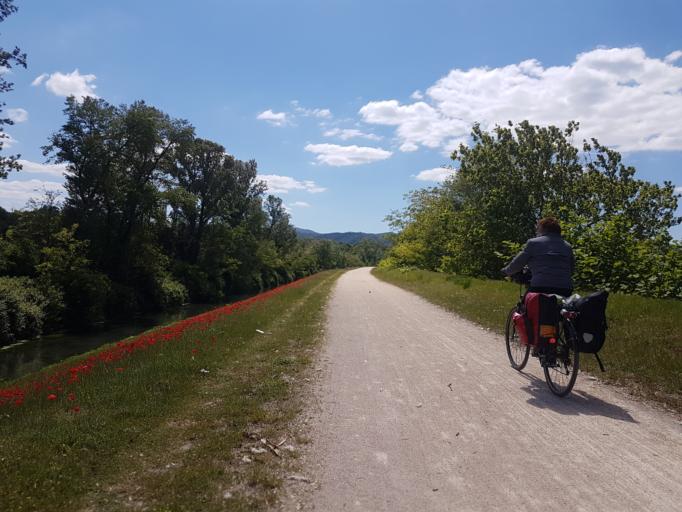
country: FR
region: Rhone-Alpes
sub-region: Departement de l'Ardeche
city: Mauves
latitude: 45.0469
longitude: 4.8567
